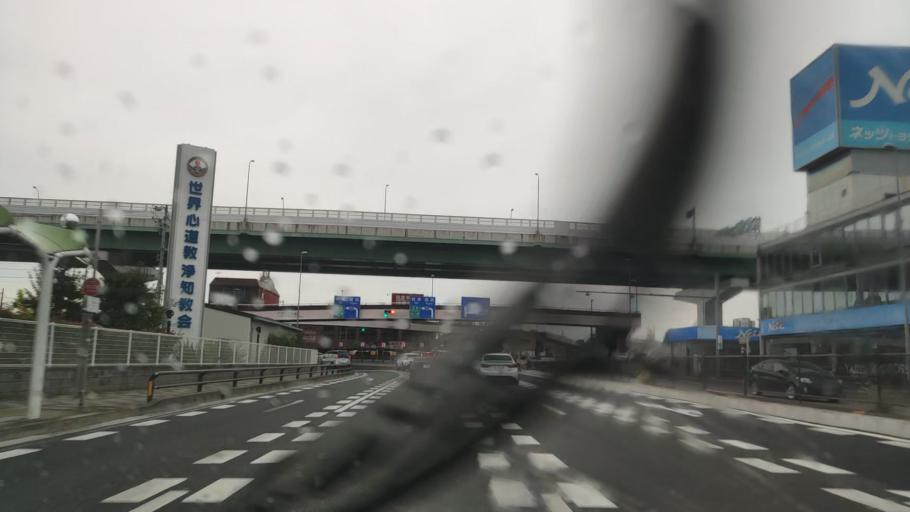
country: JP
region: Aichi
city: Nagoya-shi
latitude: 35.2022
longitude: 136.8814
